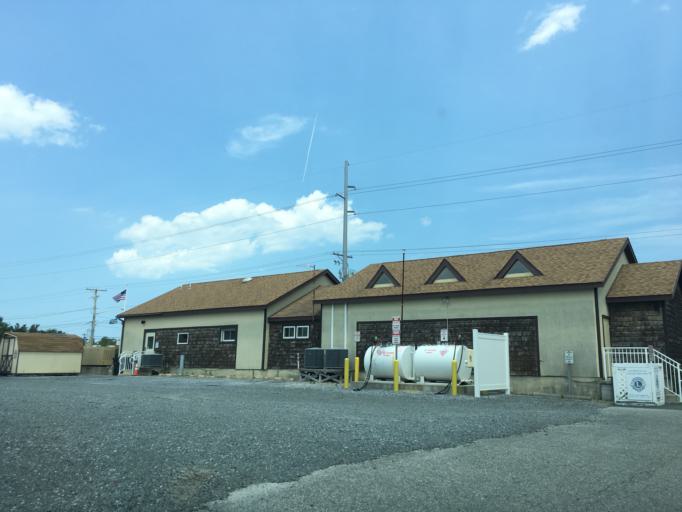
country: US
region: Delaware
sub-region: Sussex County
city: Bethany Beach
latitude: 38.4577
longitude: -75.0528
